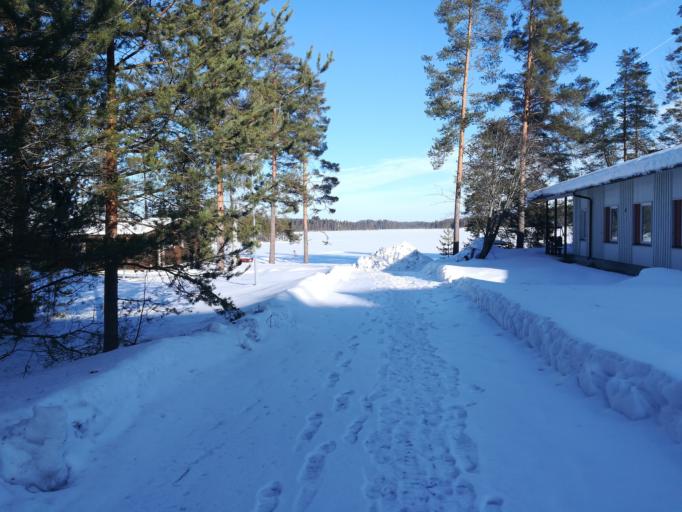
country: FI
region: Southern Savonia
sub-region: Savonlinna
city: Savonlinna
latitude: 61.8078
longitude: 29.0782
